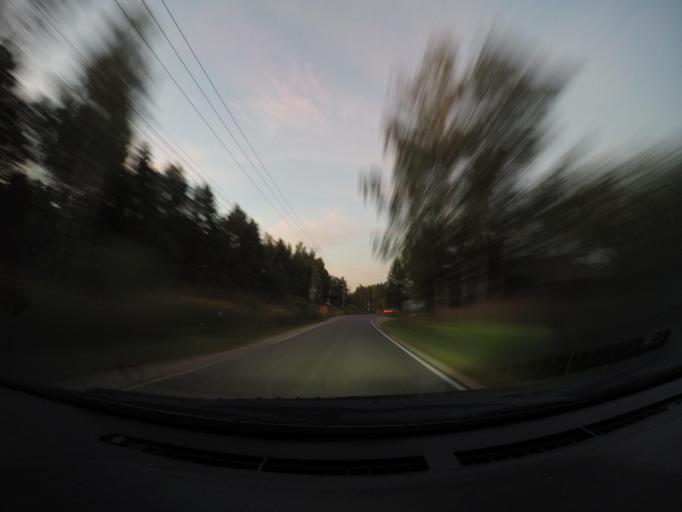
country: RU
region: Moskovskaya
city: Rechitsy
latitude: 55.5468
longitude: 38.4511
